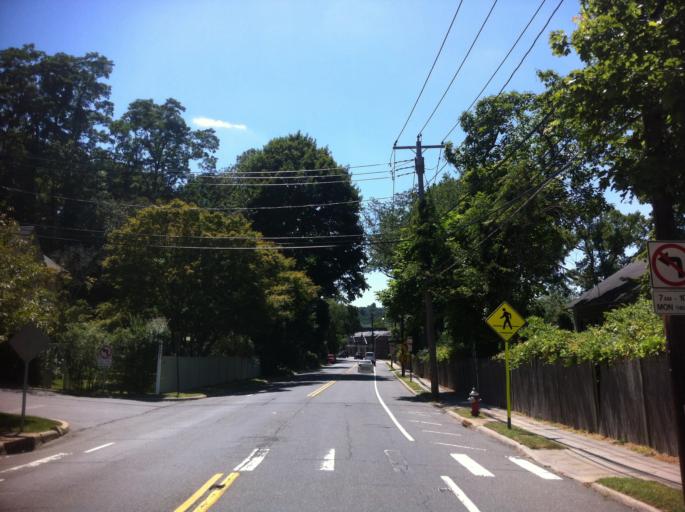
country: US
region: New York
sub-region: Nassau County
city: Roslyn
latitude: 40.8089
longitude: -73.6458
